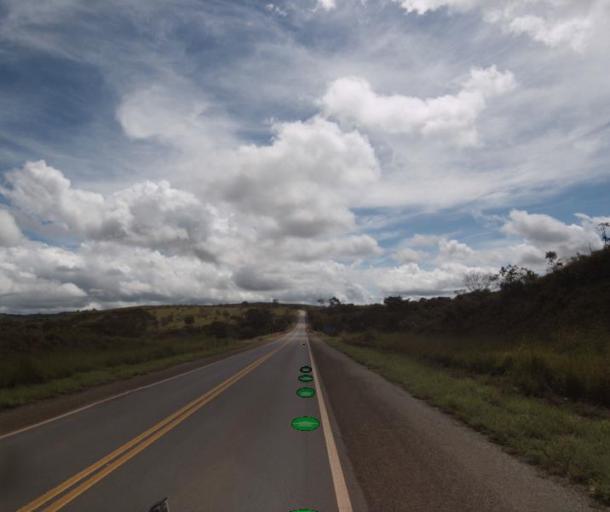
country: BR
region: Federal District
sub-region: Brasilia
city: Brasilia
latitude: -15.7504
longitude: -48.3500
